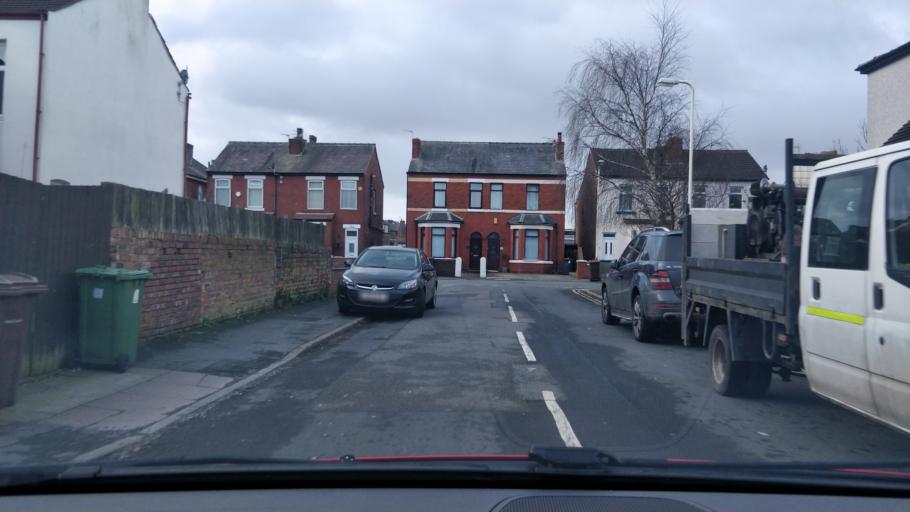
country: GB
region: England
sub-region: Sefton
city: Southport
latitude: 53.6319
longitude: -3.0023
